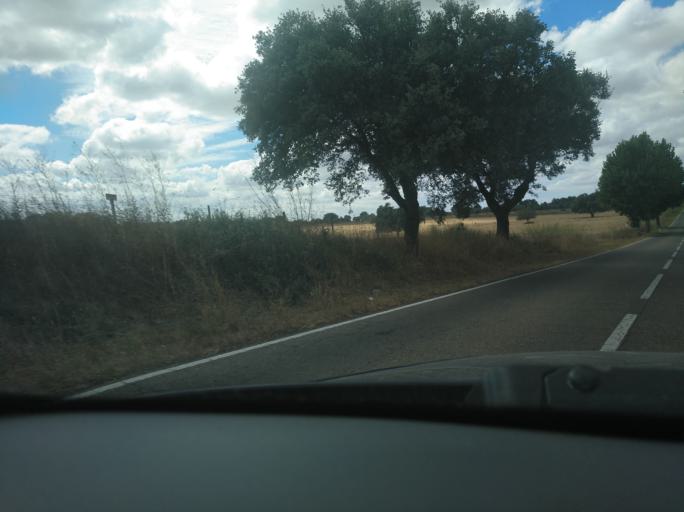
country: PT
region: Portalegre
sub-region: Arronches
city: Arronches
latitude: 39.0433
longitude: -7.4264
